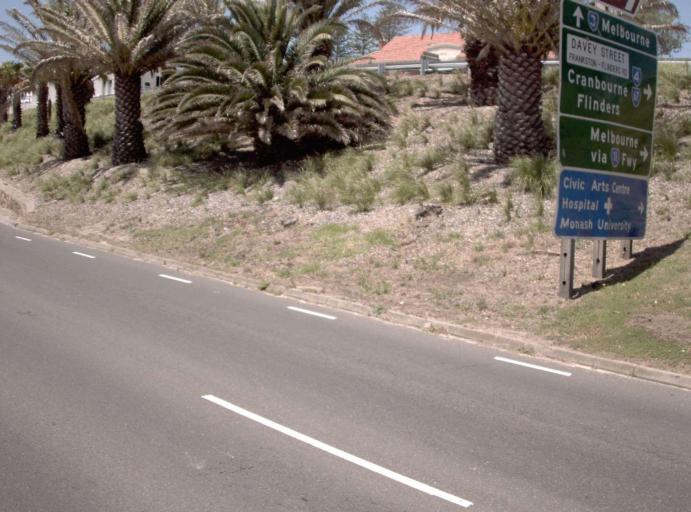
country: AU
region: Victoria
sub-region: Frankston
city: Frankston
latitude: -38.1461
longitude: 145.1190
